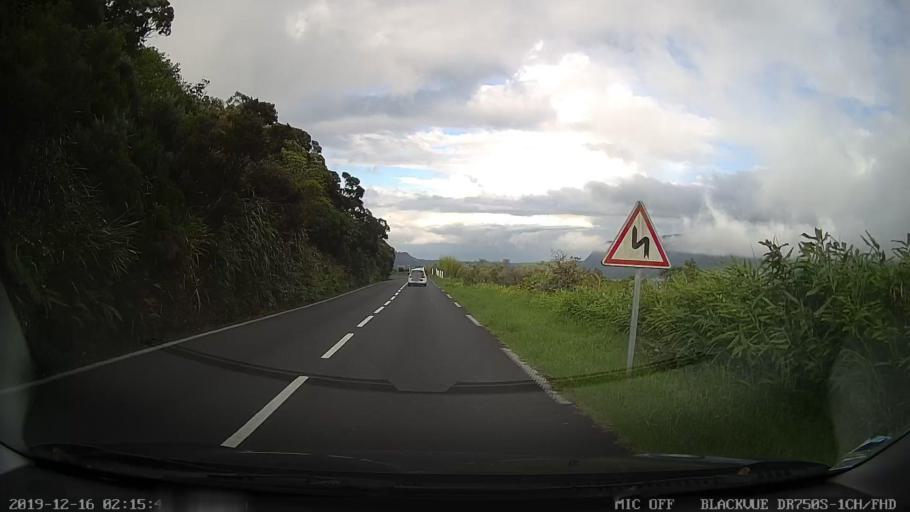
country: RE
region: Reunion
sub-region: Reunion
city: Cilaos
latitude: -21.1570
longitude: 55.5988
